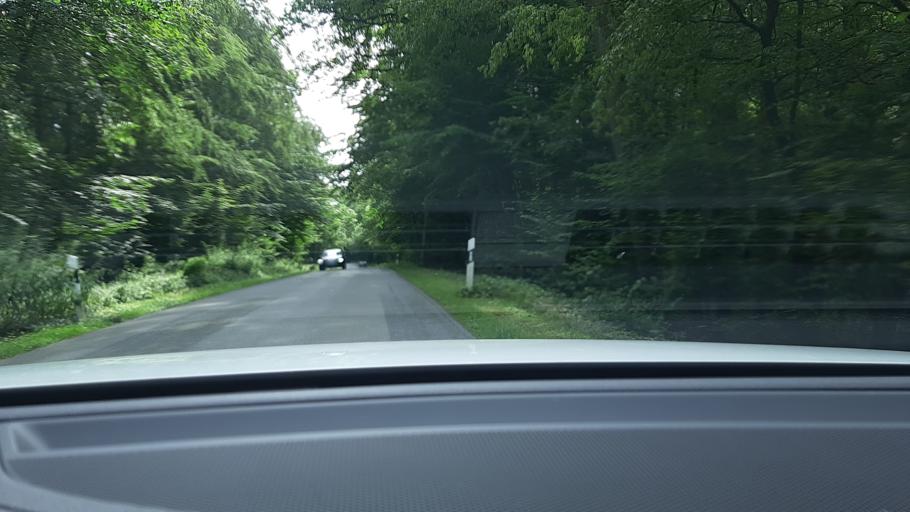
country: DE
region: Schleswig-Holstein
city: Reinfeld
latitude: 53.8500
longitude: 10.4726
